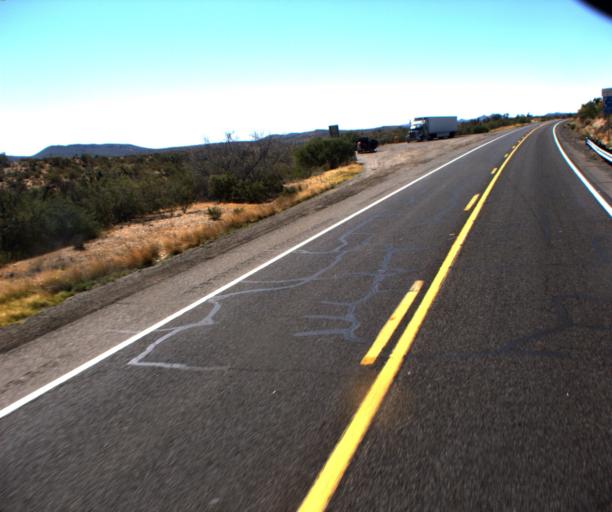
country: US
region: Arizona
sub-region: Yavapai County
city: Congress
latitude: 34.2320
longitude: -113.0712
